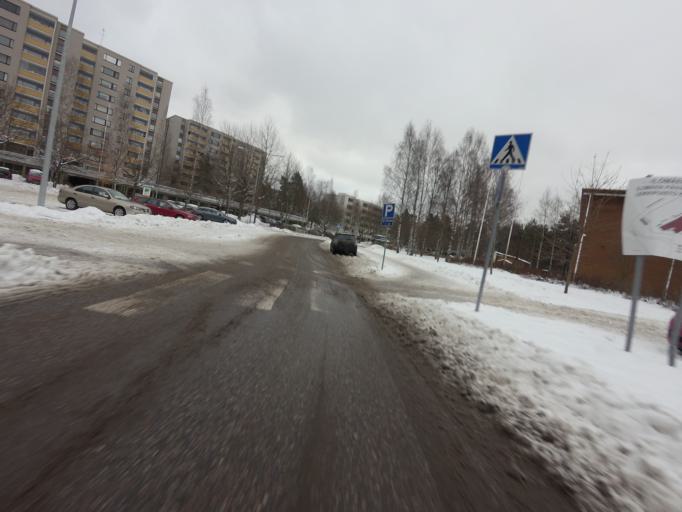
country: FI
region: Uusimaa
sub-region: Helsinki
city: Vantaa
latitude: 60.1812
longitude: 25.0587
